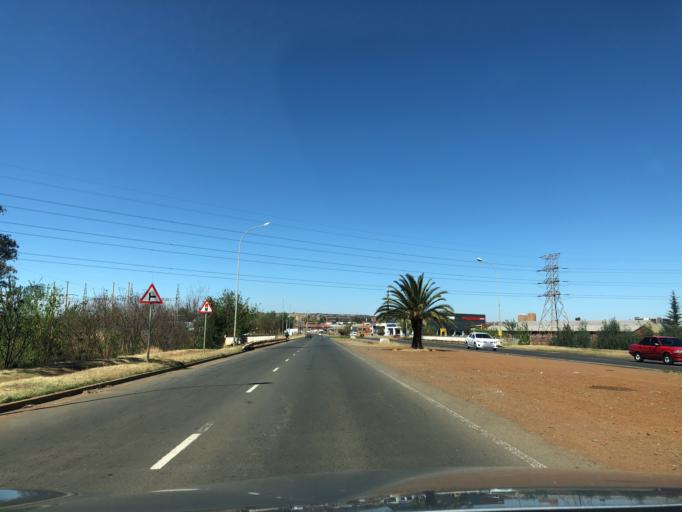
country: ZA
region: KwaZulu-Natal
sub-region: Amajuba District Municipality
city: Newcastle
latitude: -27.7465
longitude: 29.9375
